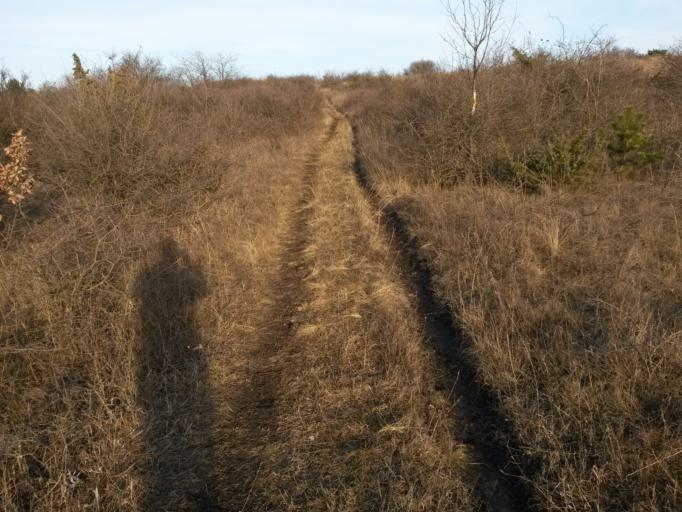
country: HU
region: Pest
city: Perbal
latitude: 47.5902
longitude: 18.7225
